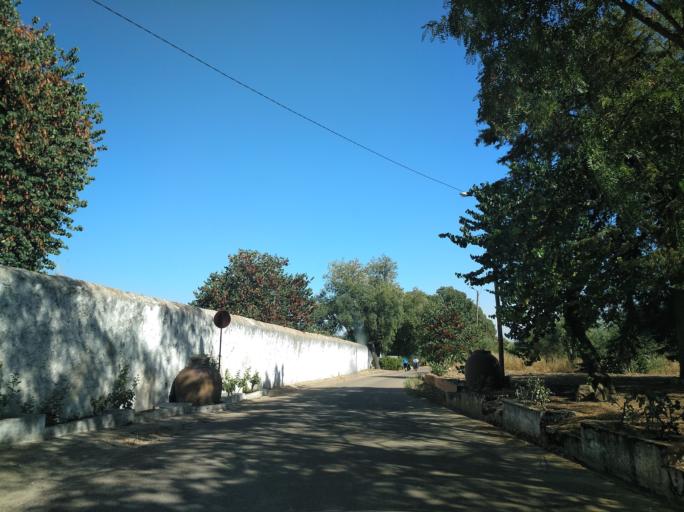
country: PT
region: Portalegre
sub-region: Elvas
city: Elvas
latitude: 38.9447
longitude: -7.2041
